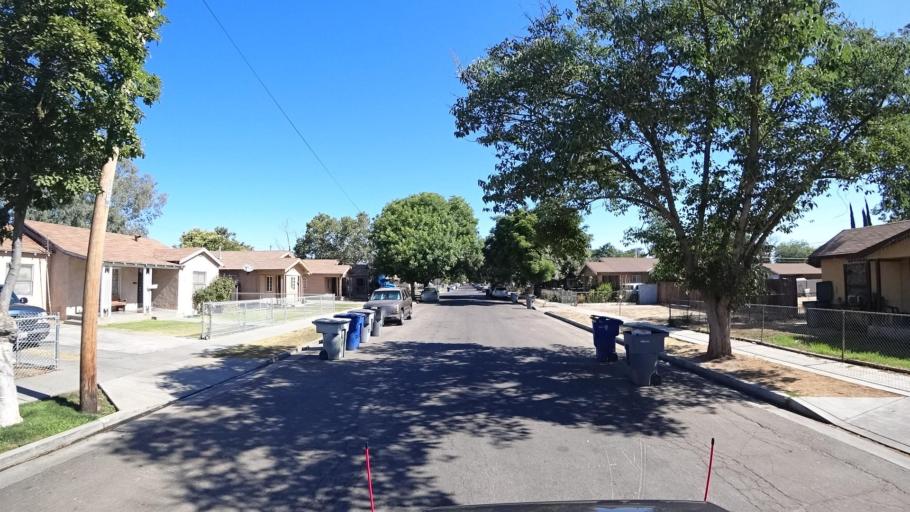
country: US
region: California
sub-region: Fresno County
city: Fresno
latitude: 36.7172
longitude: -119.7897
